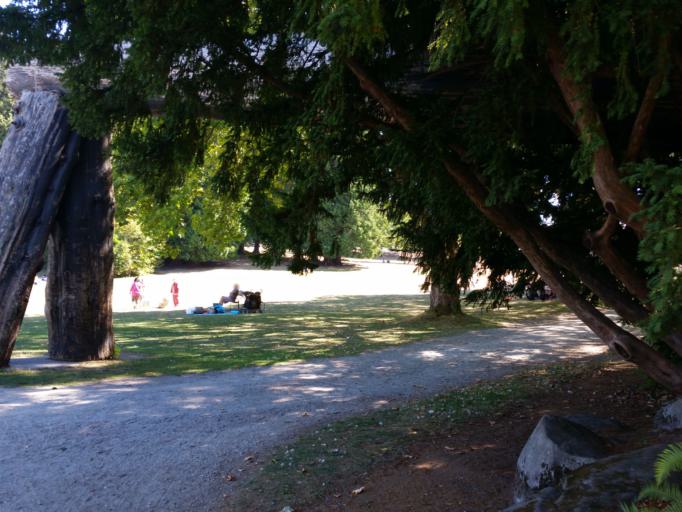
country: CA
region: British Columbia
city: West End
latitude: 49.3026
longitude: -123.1306
